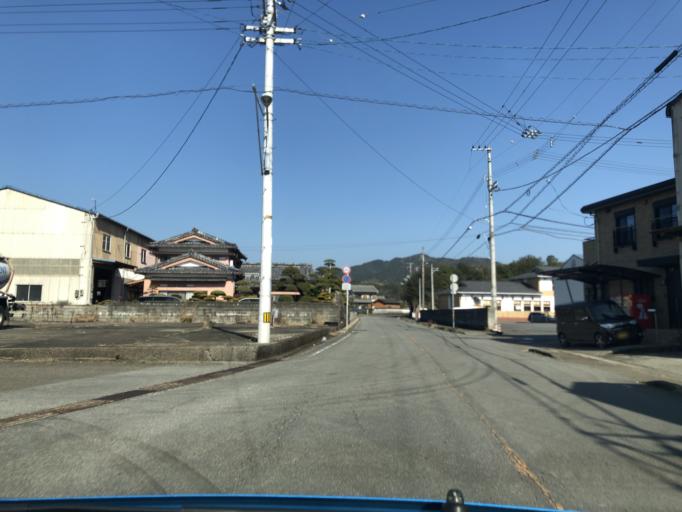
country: JP
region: Kochi
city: Sukumo
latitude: 32.9252
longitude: 132.6959
